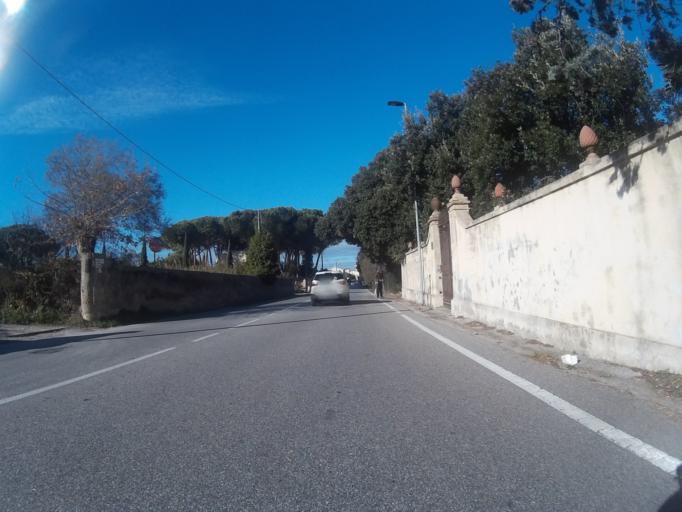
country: IT
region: Tuscany
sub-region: Provincia di Livorno
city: Livorno
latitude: 43.5102
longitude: 10.3315
